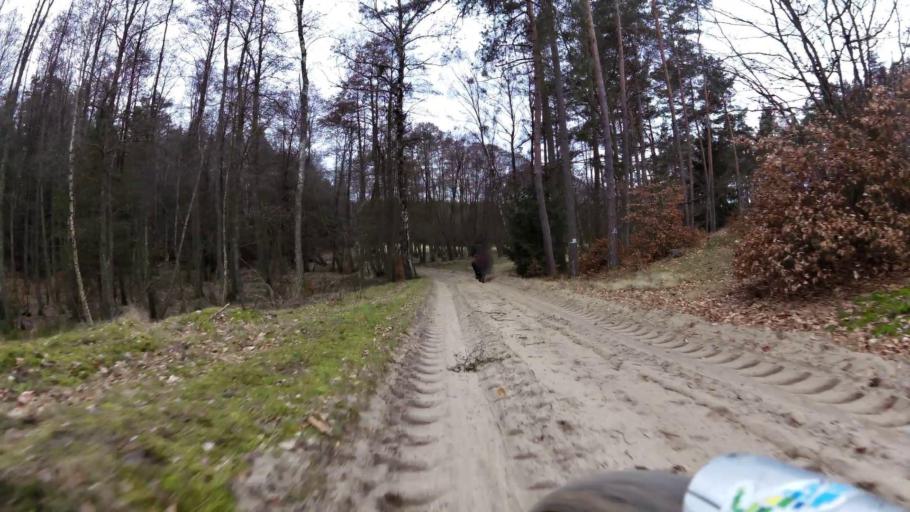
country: PL
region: Pomeranian Voivodeship
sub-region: Powiat bytowski
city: Trzebielino
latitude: 54.1291
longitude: 17.1360
